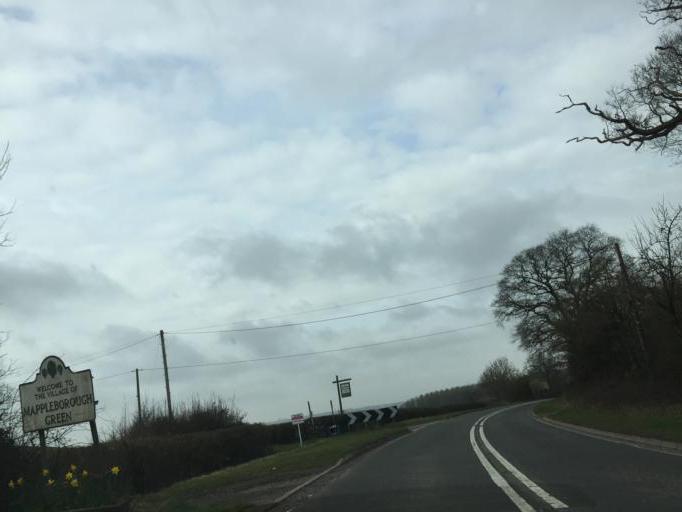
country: GB
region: England
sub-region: Warwickshire
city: Studley
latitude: 52.2988
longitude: -1.8668
